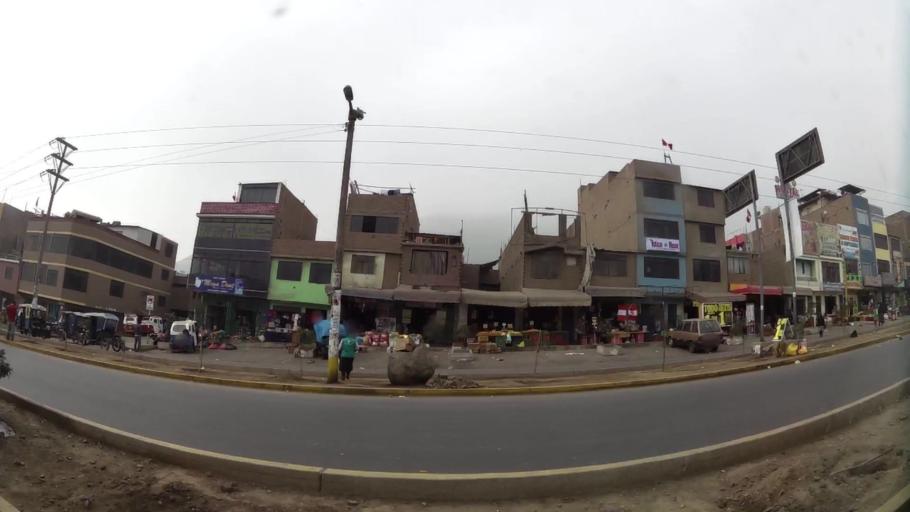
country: PE
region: Lima
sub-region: Lima
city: Chaclacayo
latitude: -12.0095
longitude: -76.8228
